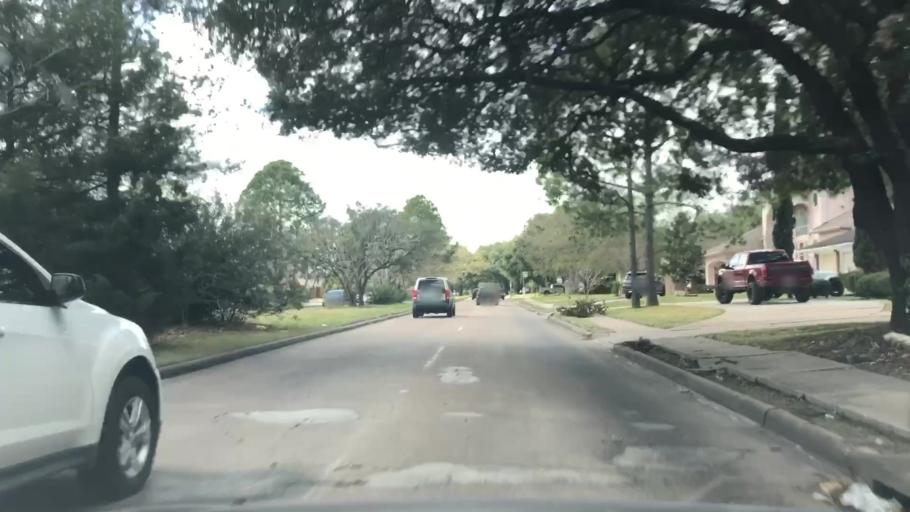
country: US
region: Texas
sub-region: Harris County
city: Bellaire
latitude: 29.6892
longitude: -95.4809
